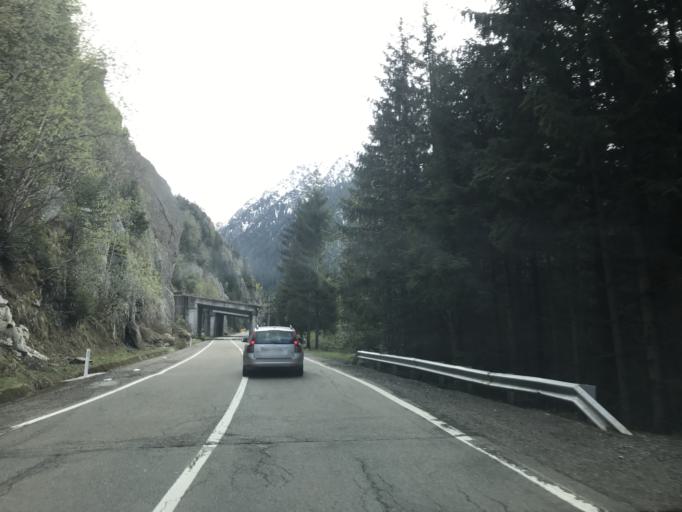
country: RO
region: Sibiu
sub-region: Comuna Cartisoara
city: Cartisoara
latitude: 45.6452
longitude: 24.6054
